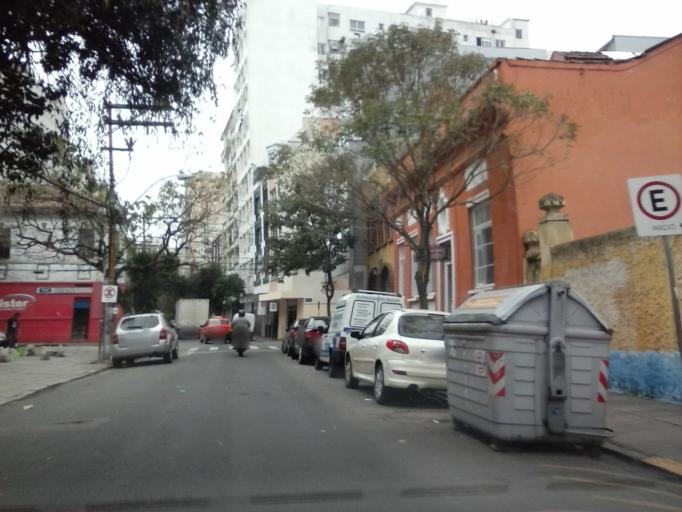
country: BR
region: Rio Grande do Sul
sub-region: Porto Alegre
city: Porto Alegre
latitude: -30.0360
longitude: -51.2315
